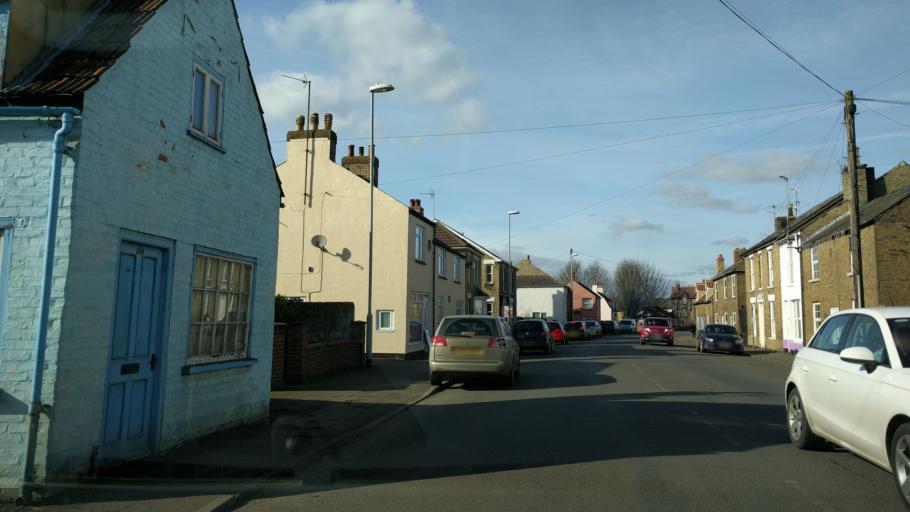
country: GB
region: England
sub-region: Cambridgeshire
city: Chatteris
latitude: 52.4595
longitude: 0.0454
